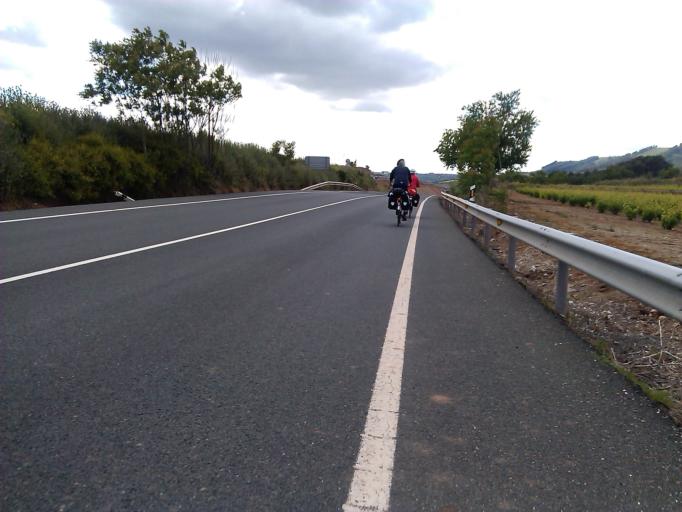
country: ES
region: La Rioja
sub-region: Provincia de La Rioja
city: Azofra
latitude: 42.4335
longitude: -2.8002
